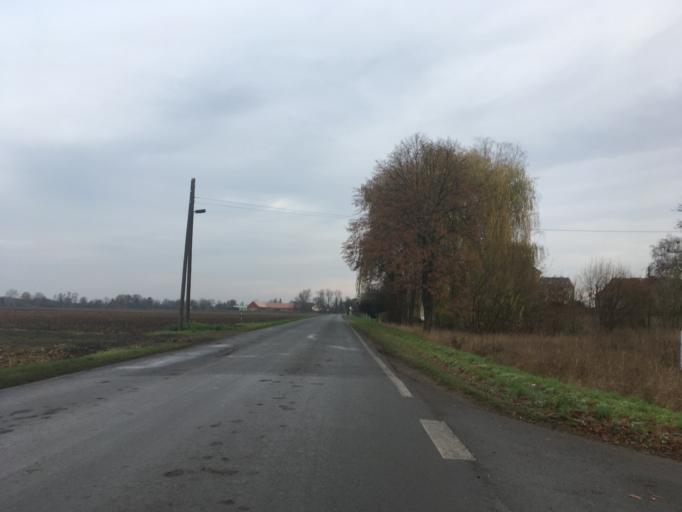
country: DE
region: Brandenburg
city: Letschin
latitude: 52.6507
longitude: 14.3607
